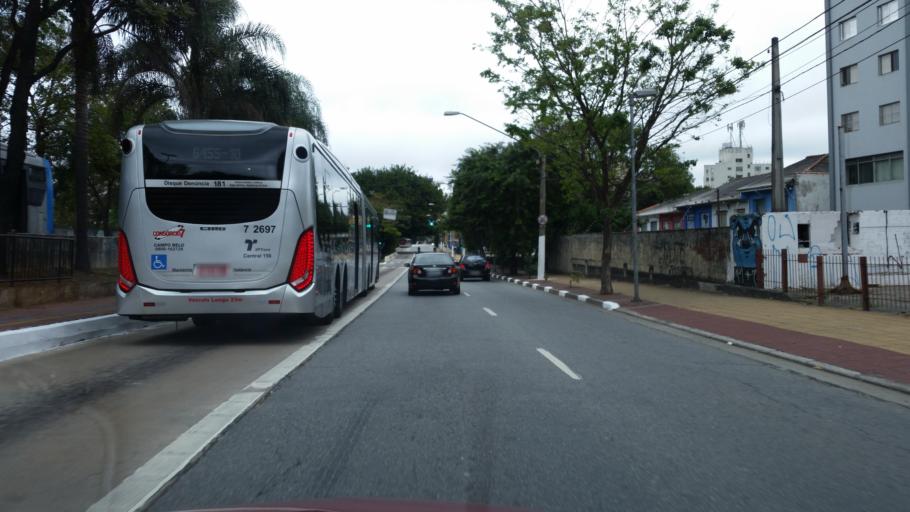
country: BR
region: Sao Paulo
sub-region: Diadema
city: Diadema
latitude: -23.6384
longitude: -46.6951
